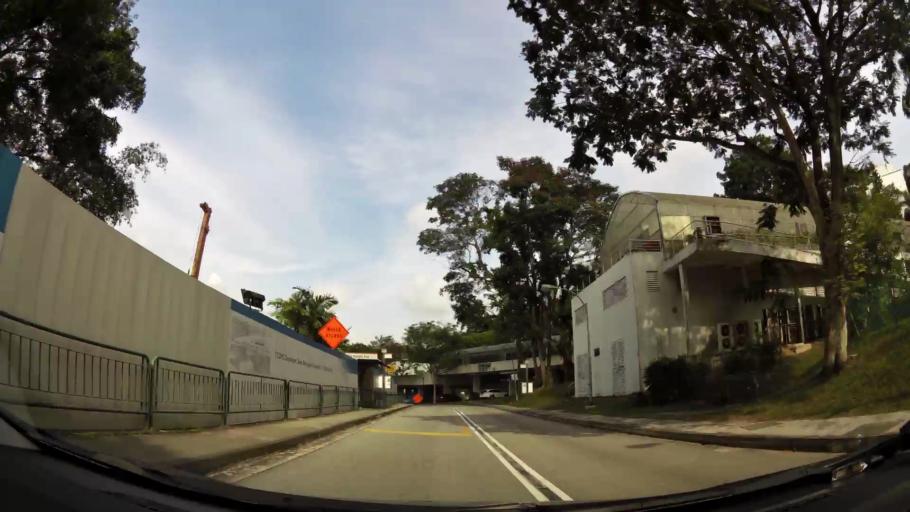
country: SG
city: Singapore
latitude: 1.2934
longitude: 103.7772
